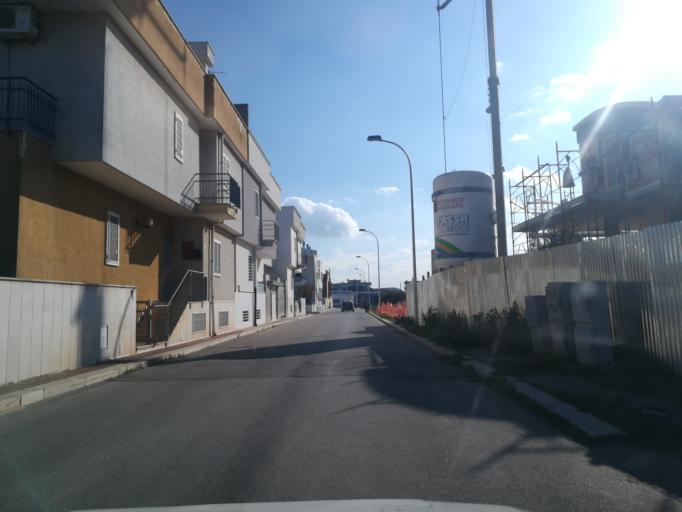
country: IT
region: Apulia
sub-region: Provincia di Bari
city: Modugno
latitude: 41.0772
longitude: 16.7786
